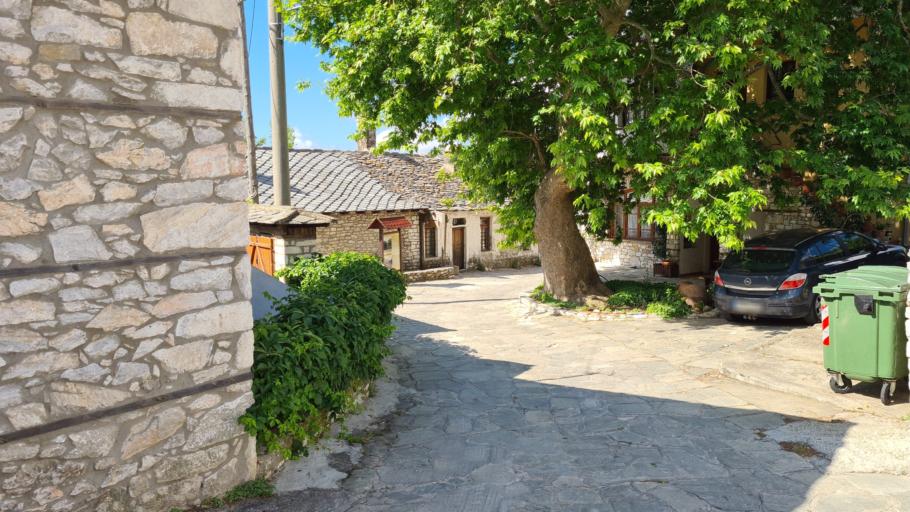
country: GR
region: East Macedonia and Thrace
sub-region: Nomos Kavalas
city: Potamia
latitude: 40.6609
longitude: 24.6957
